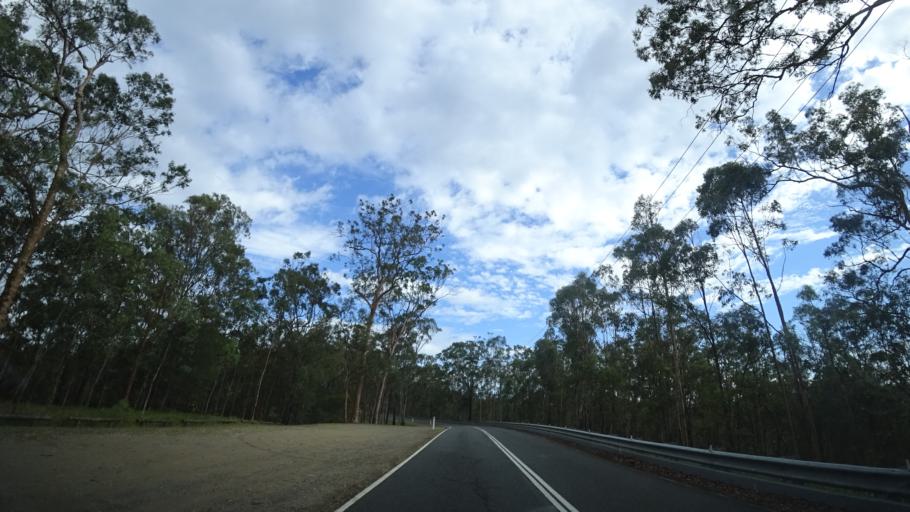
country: AU
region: Queensland
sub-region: Brisbane
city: Taringa
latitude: -27.4816
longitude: 152.9539
